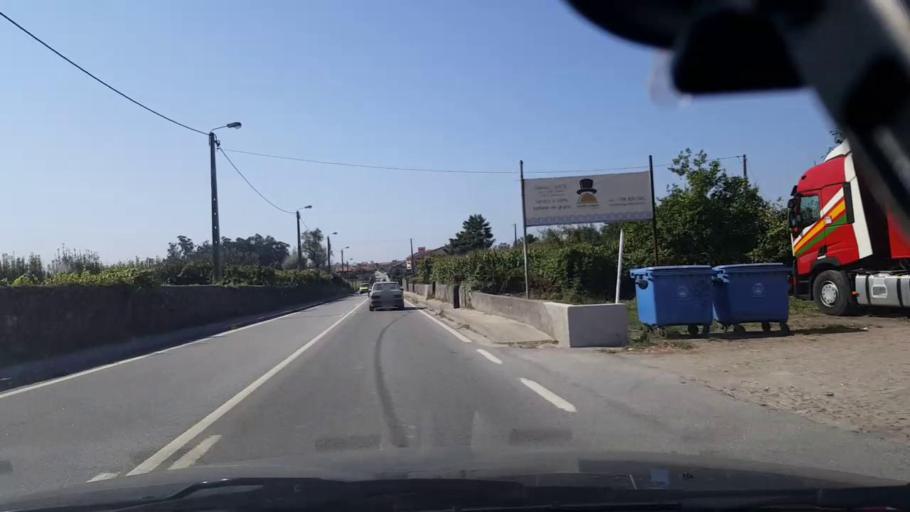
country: PT
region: Porto
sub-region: Povoa de Varzim
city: Pedroso
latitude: 41.3983
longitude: -8.6842
